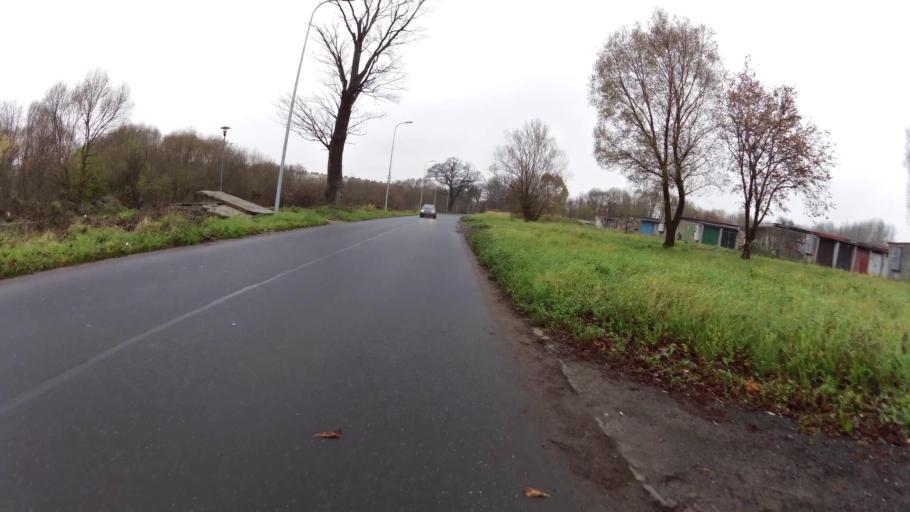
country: PL
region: West Pomeranian Voivodeship
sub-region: Koszalin
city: Koszalin
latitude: 54.2036
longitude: 16.1716
